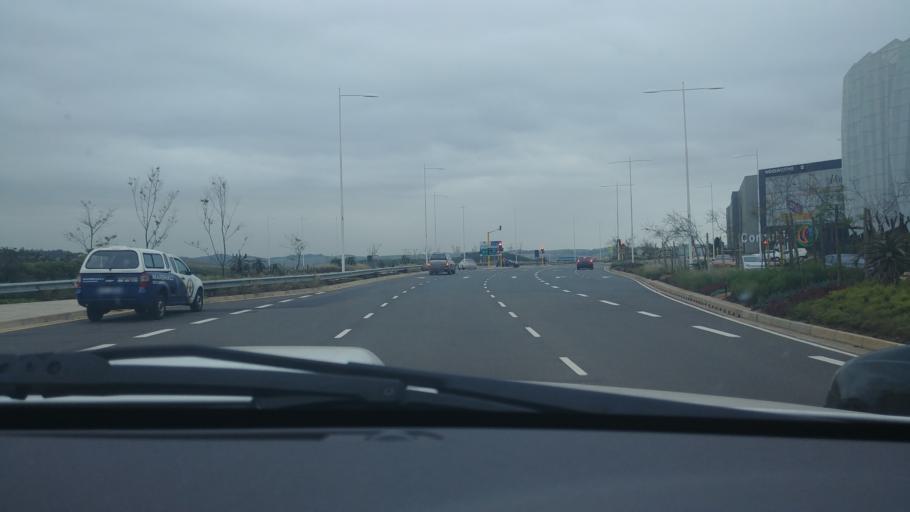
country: ZA
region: KwaZulu-Natal
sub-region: eThekwini Metropolitan Municipality
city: Durban
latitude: -29.7104
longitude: 31.0527
